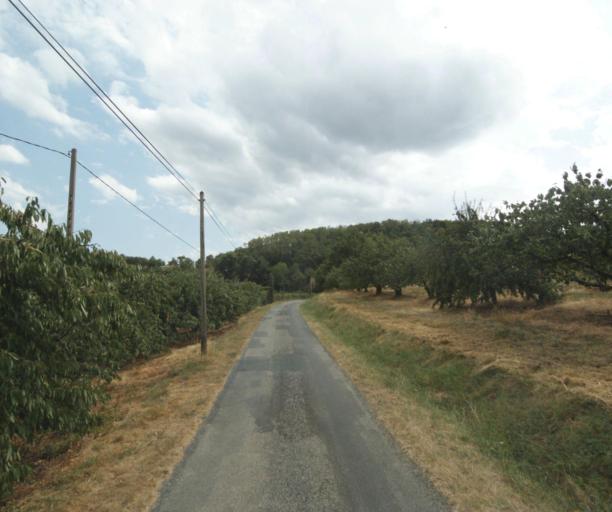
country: FR
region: Rhone-Alpes
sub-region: Departement du Rhone
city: Bully
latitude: 45.8815
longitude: 4.5703
